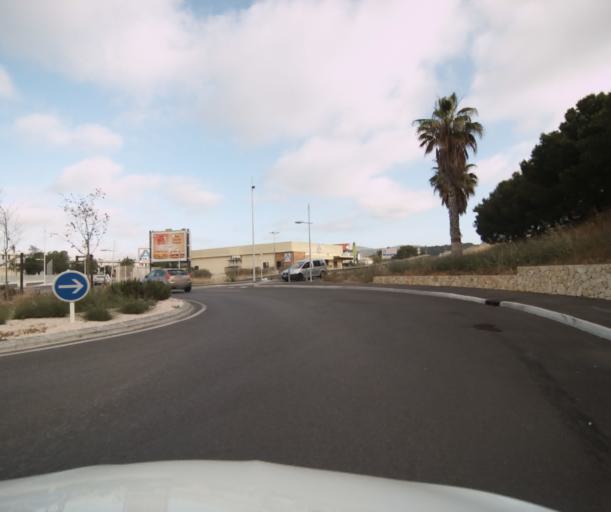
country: FR
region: Provence-Alpes-Cote d'Azur
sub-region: Departement du Var
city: Six-Fours-les-Plages
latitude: 43.1143
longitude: 5.8567
